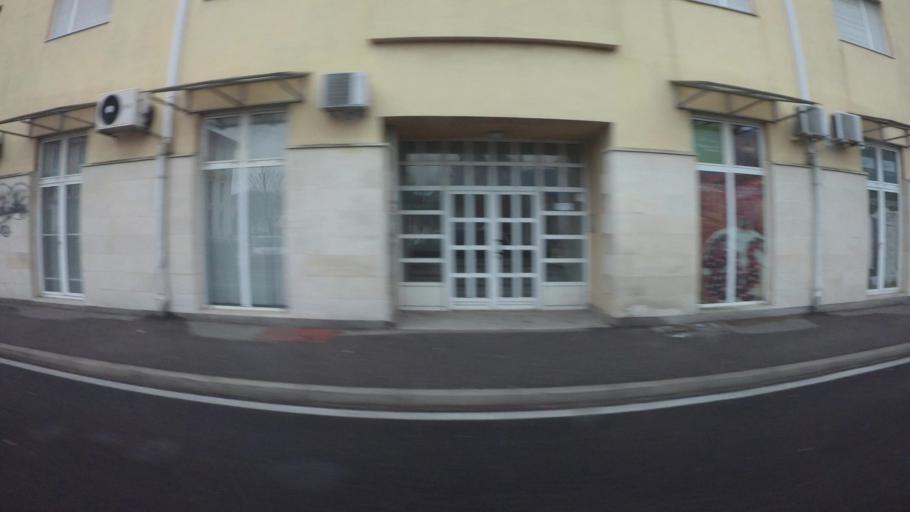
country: BA
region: Federation of Bosnia and Herzegovina
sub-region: Hercegovacko-Bosanski Kanton
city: Mostar
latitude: 43.3419
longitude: 17.8082
